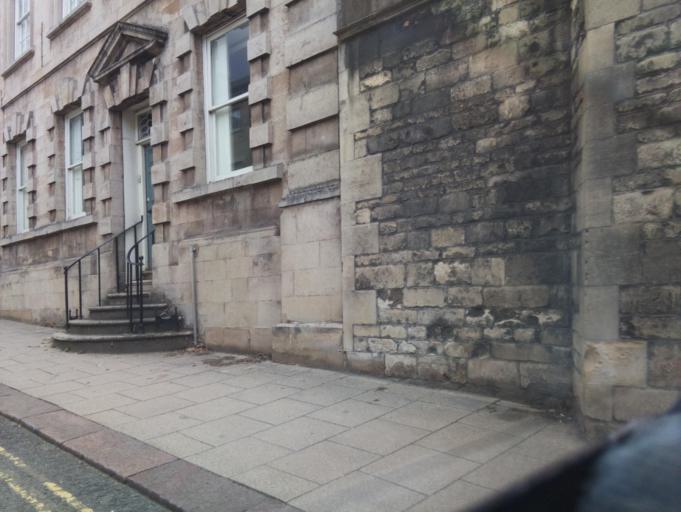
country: GB
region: England
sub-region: Lincolnshire
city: Stamford
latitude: 52.6494
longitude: -0.4779
